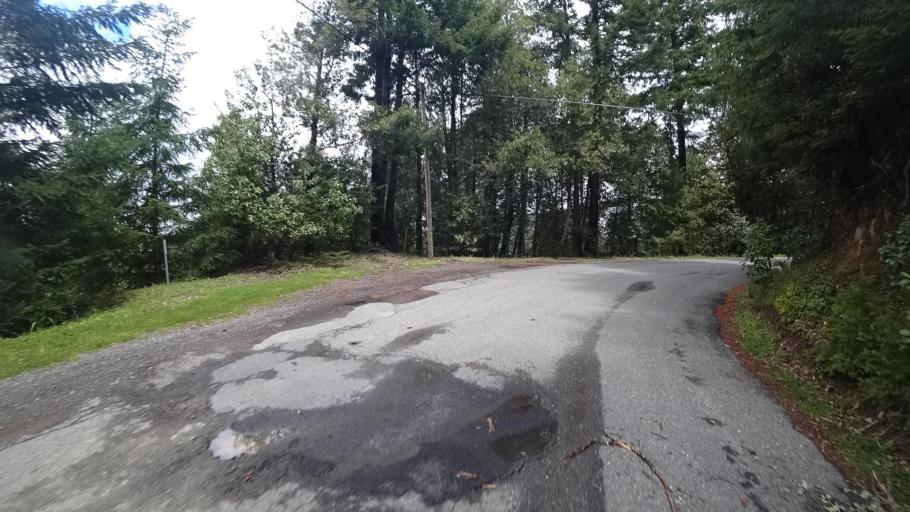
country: US
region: California
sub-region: Humboldt County
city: Blue Lake
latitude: 40.8806
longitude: -123.8818
